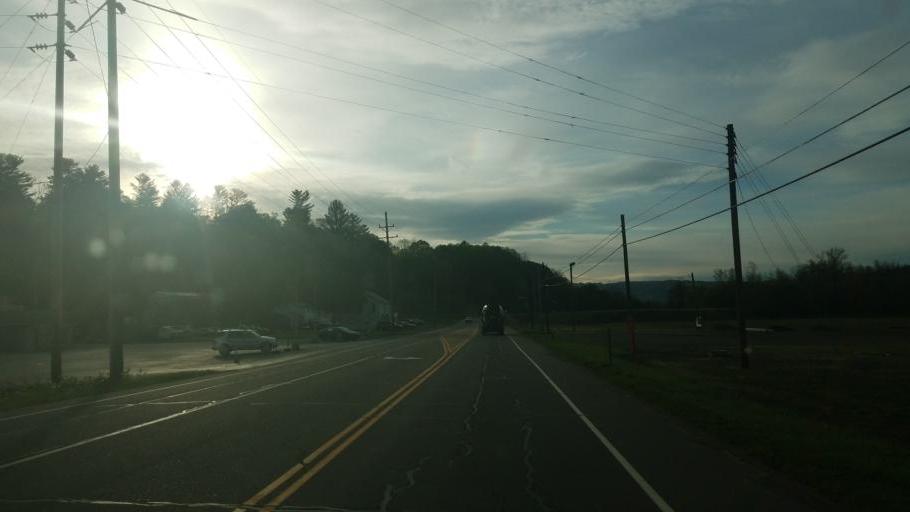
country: US
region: New York
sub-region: Steuben County
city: Hornell
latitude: 42.3341
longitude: -77.6780
